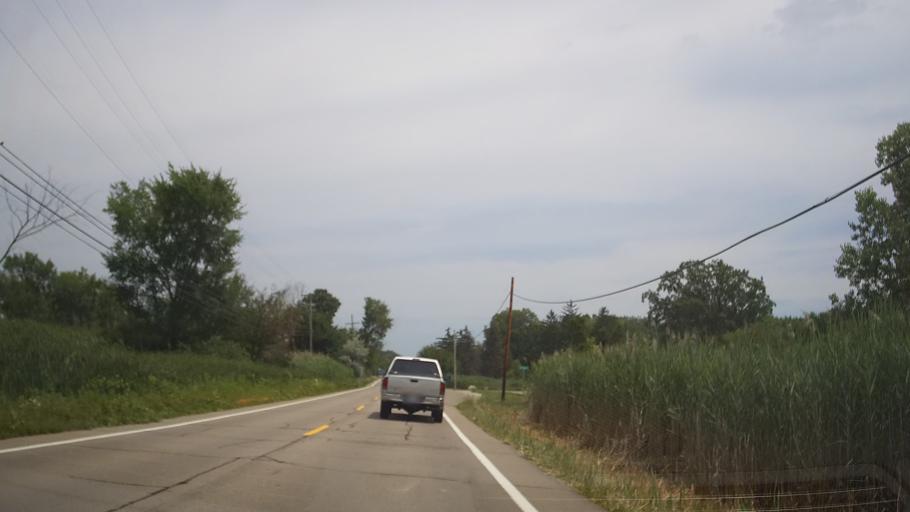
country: US
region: Michigan
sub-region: Oakland County
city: Troy
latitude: 42.6072
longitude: -83.1191
